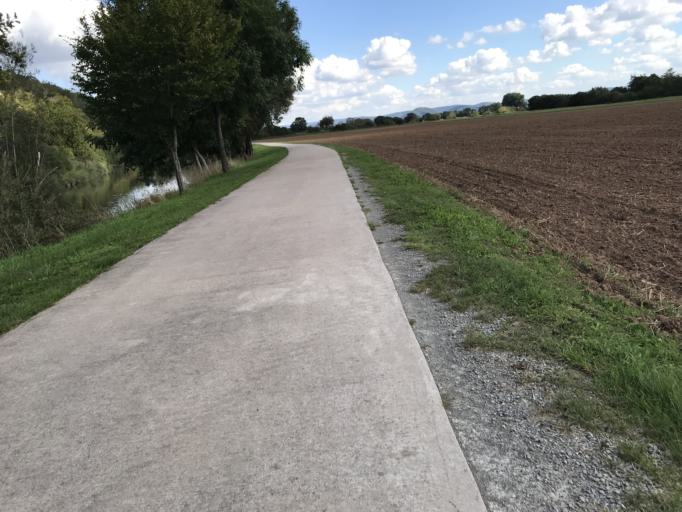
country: DE
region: Hesse
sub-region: Regierungsbezirk Kassel
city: Bad Sooden-Allendorf
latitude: 51.2171
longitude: 9.9920
